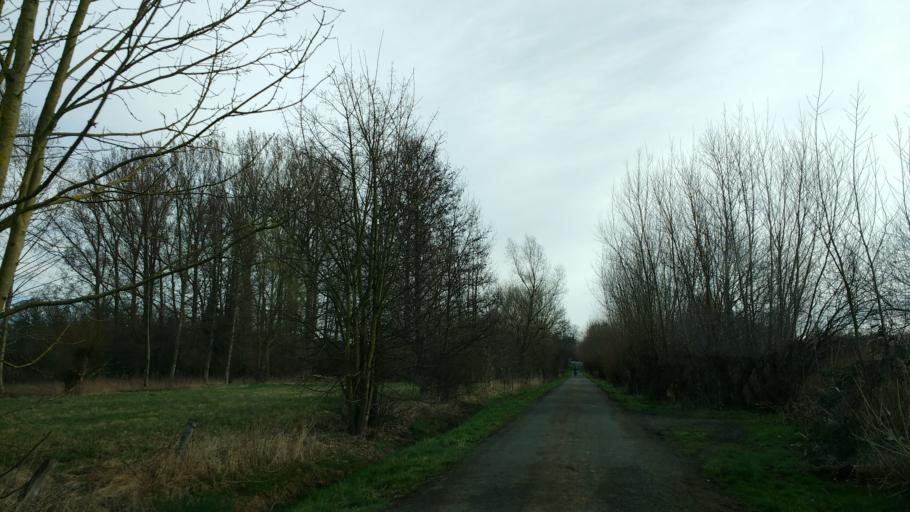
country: DE
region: North Rhine-Westphalia
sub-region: Regierungsbezirk Detmold
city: Paderborn
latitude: 51.7472
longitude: 8.7359
